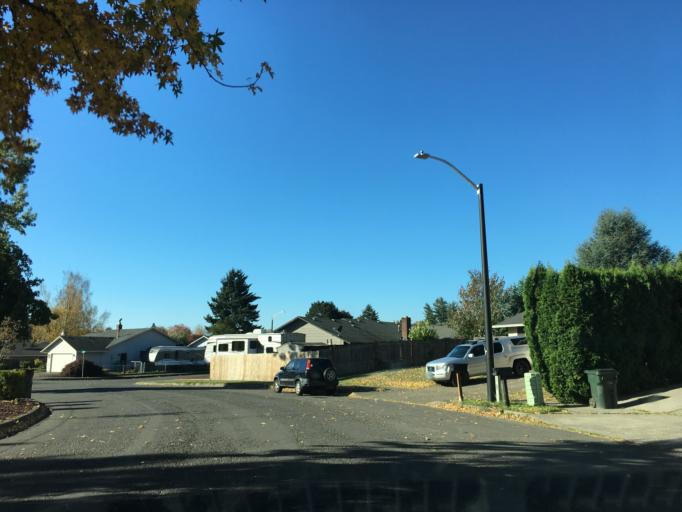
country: US
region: Oregon
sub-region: Multnomah County
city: Wood Village
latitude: 45.5160
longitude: -122.4171
